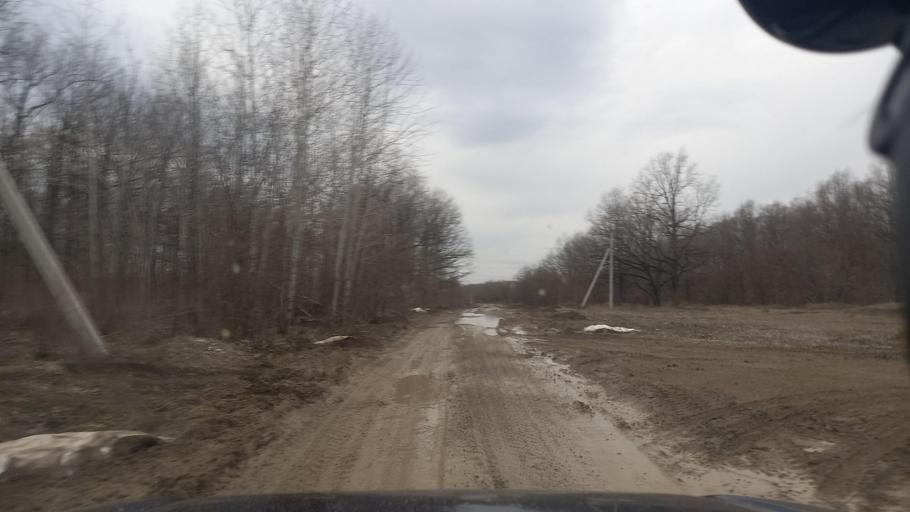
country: RU
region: Krasnodarskiy
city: Novodmitriyevskaya
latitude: 44.7514
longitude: 39.0034
